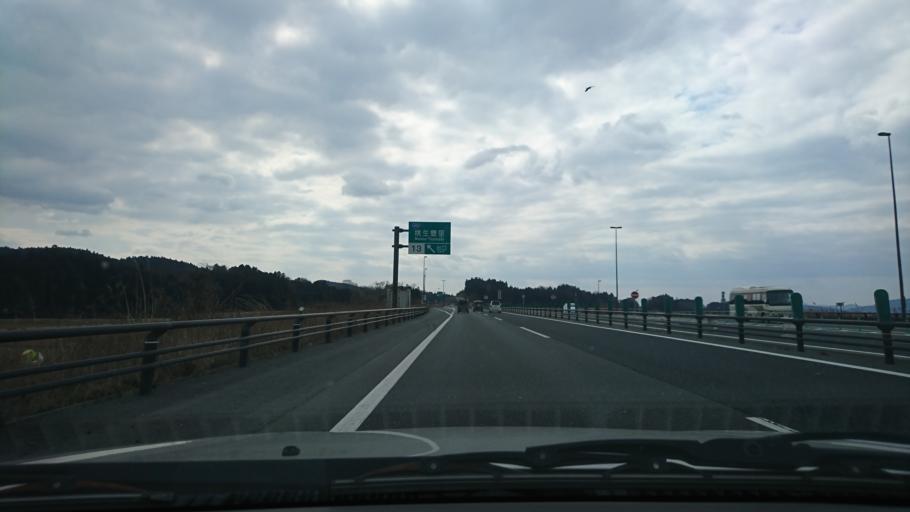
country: JP
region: Miyagi
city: Wakuya
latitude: 38.5639
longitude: 141.2718
